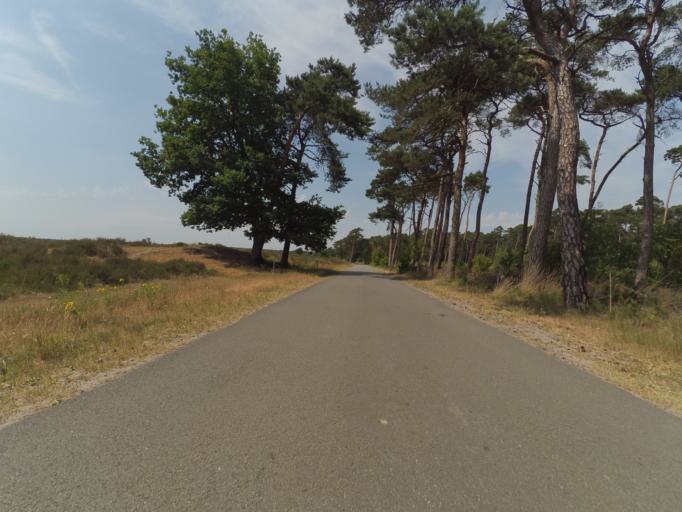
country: BE
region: Flanders
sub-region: Provincie Antwerpen
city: Kalmthout
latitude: 51.4126
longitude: 4.4279
